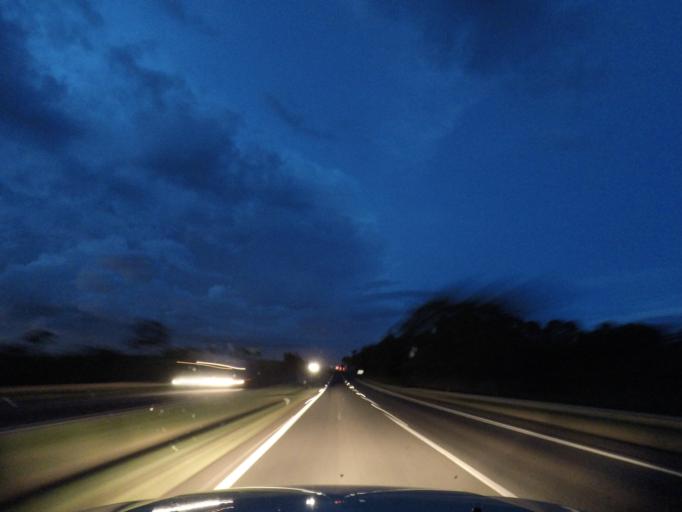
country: BR
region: Minas Gerais
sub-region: Uberlandia
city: Uberlandia
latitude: -19.2305
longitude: -48.1428
